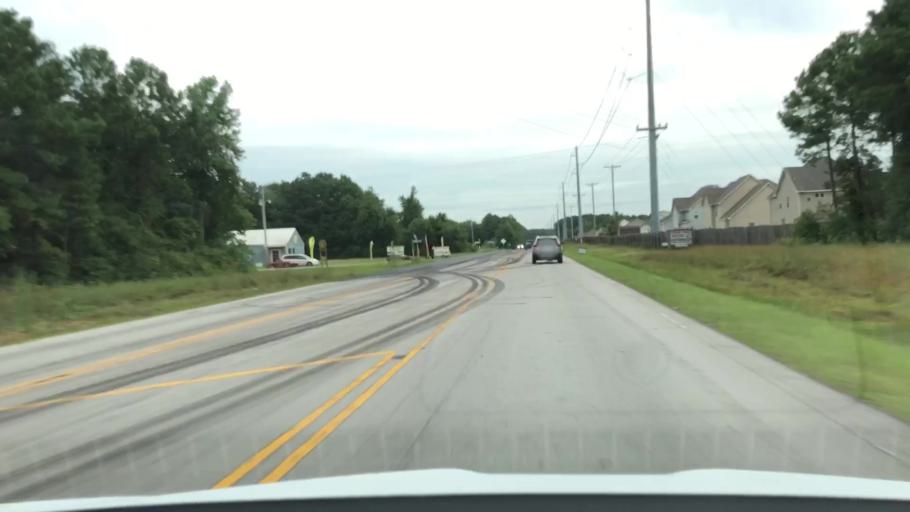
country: US
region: North Carolina
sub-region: Carteret County
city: Cape Carteret
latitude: 34.7579
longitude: -77.0942
